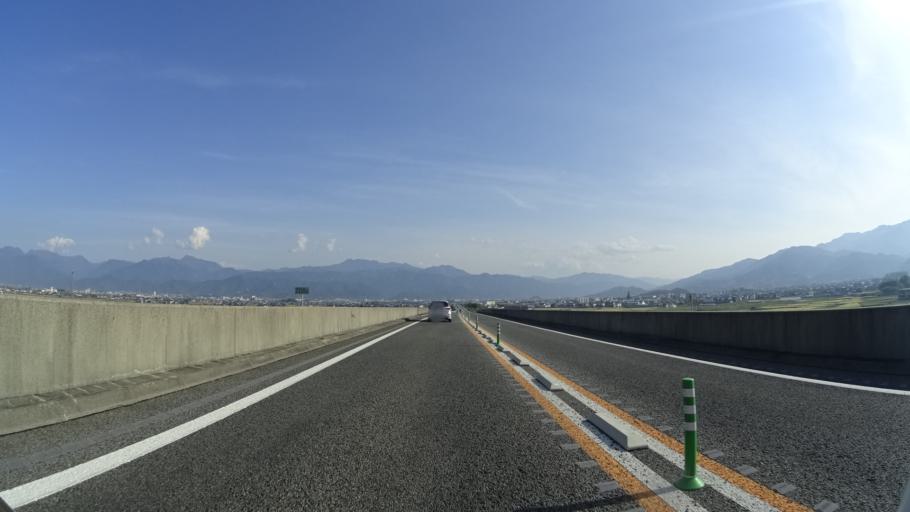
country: JP
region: Ehime
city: Saijo
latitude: 33.9492
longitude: 133.0693
